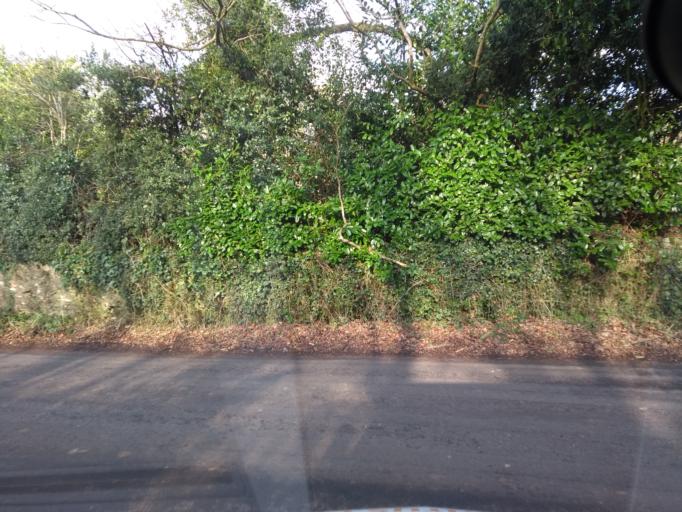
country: GB
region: England
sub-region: Somerset
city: Chard
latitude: 50.9150
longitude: -3.0364
